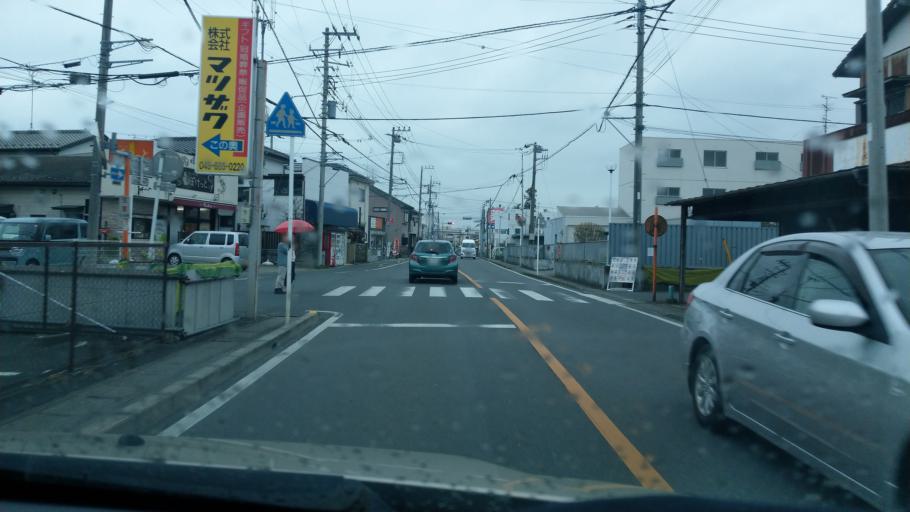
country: JP
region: Saitama
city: Iwatsuki
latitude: 35.9318
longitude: 139.6730
